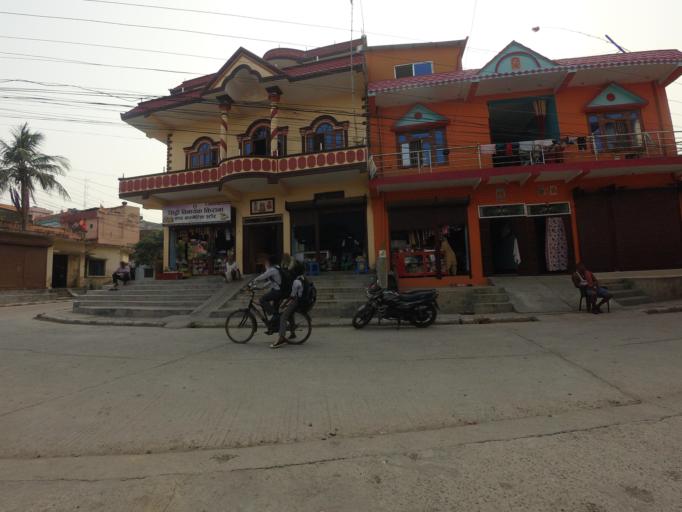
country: NP
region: Western Region
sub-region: Lumbini Zone
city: Bhairahawa
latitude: 27.5104
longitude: 83.4527
